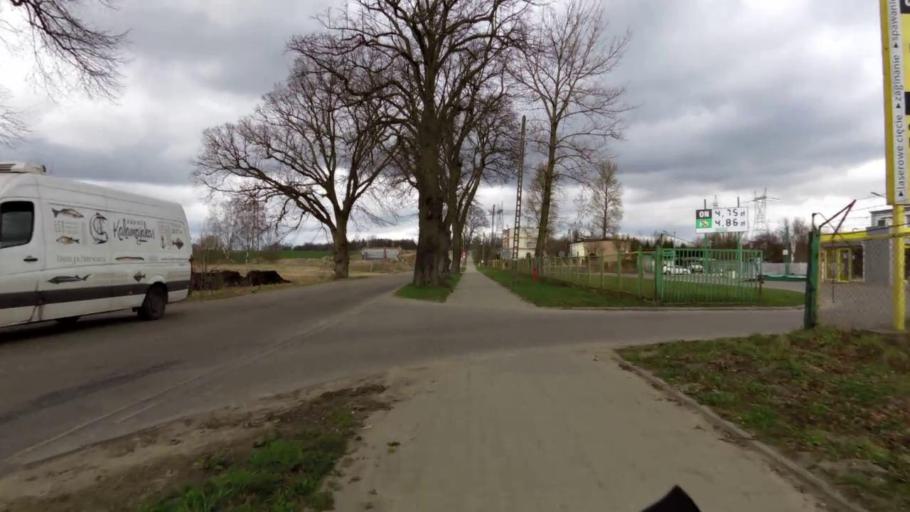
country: PL
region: West Pomeranian Voivodeship
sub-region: Powiat koszalinski
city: Sianow
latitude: 54.2367
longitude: 16.2987
